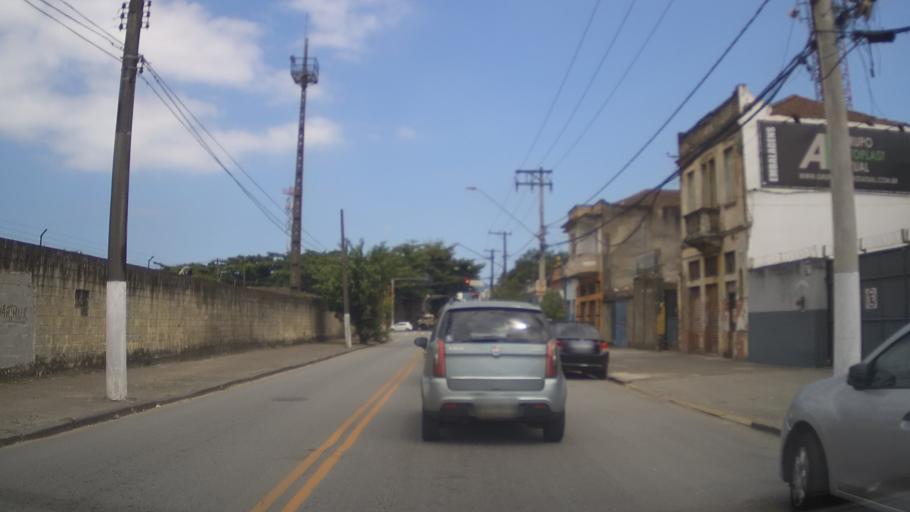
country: BR
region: Sao Paulo
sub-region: Santos
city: Santos
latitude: -23.9596
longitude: -46.3090
